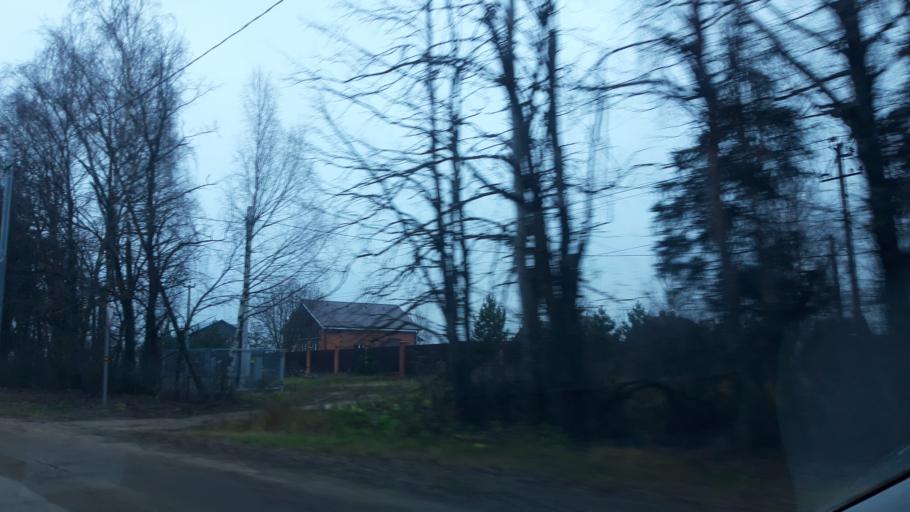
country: RU
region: Moskovskaya
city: Solnechnogorsk
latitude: 56.1321
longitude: 36.9237
